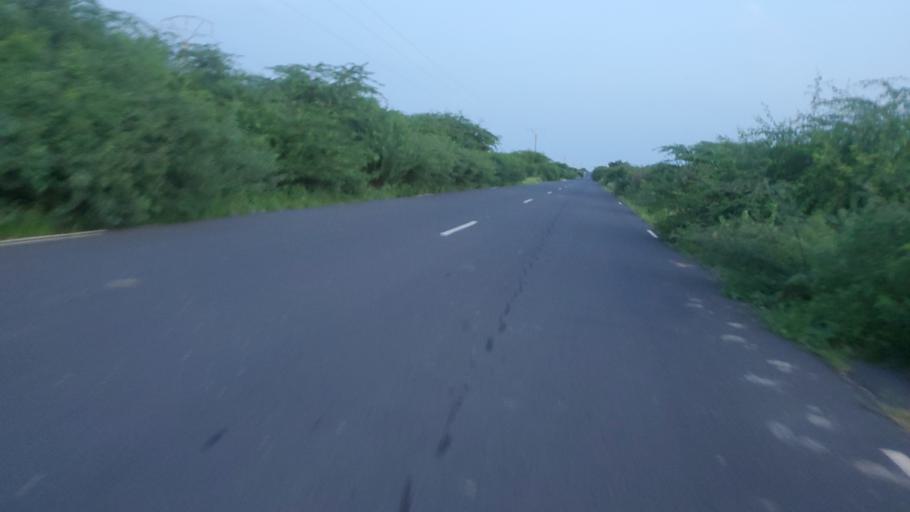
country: SN
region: Saint-Louis
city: Saint-Louis
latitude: 16.0836
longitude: -16.3932
